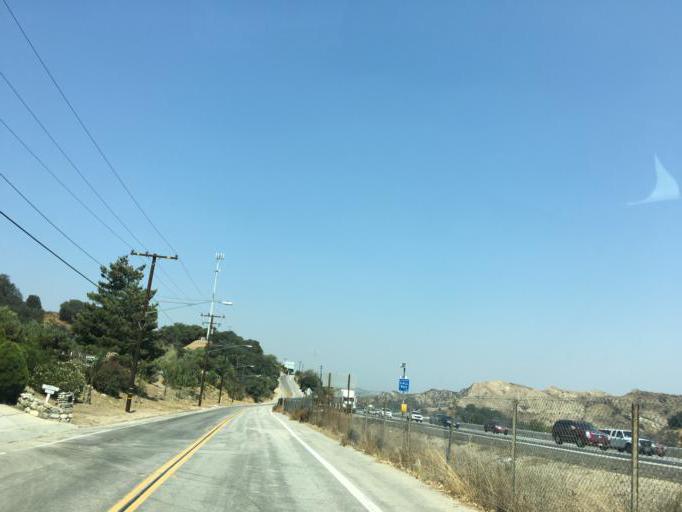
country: US
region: California
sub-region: Los Angeles County
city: Santa Clarita
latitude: 34.3419
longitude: -118.5284
